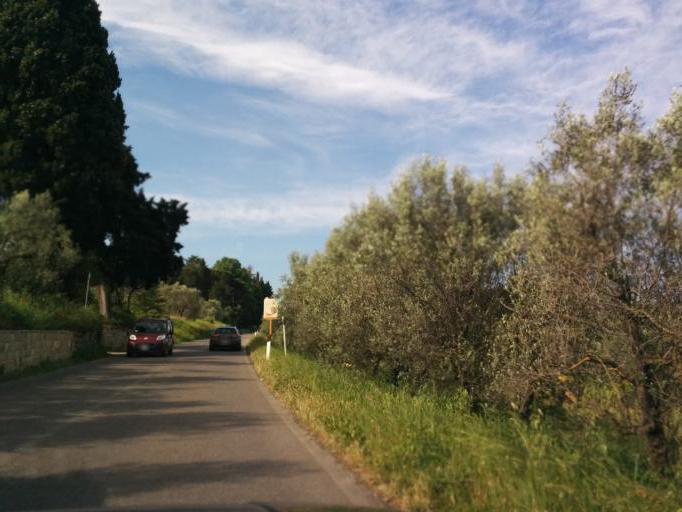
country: IT
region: Tuscany
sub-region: Province of Florence
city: San Casciano in Val di Pesa
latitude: 43.6687
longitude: 11.1966
